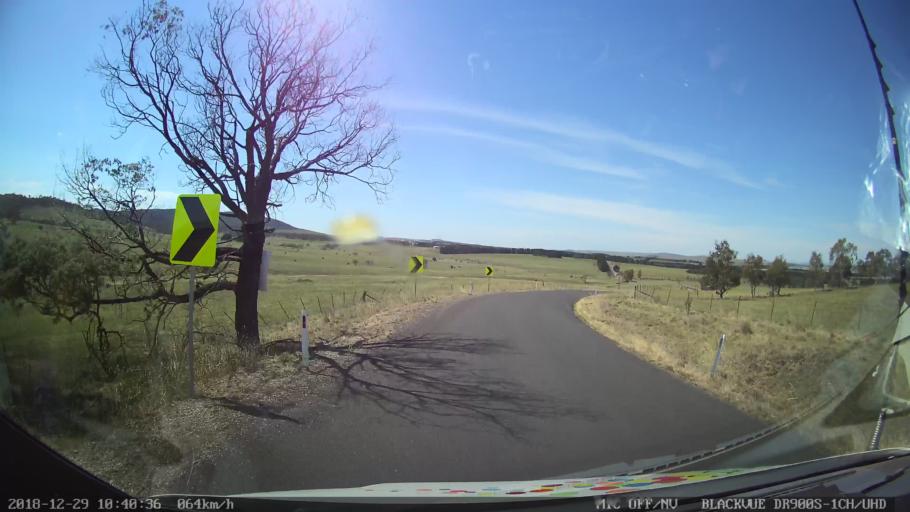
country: AU
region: New South Wales
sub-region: Palerang
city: Bungendore
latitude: -35.0166
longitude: 149.5193
